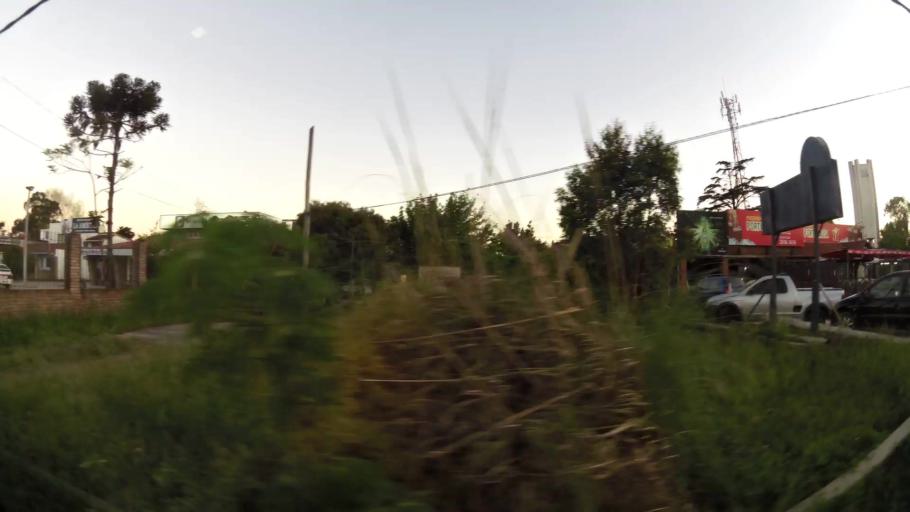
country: UY
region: Canelones
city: Colonia Nicolich
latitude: -34.8228
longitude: -55.9594
